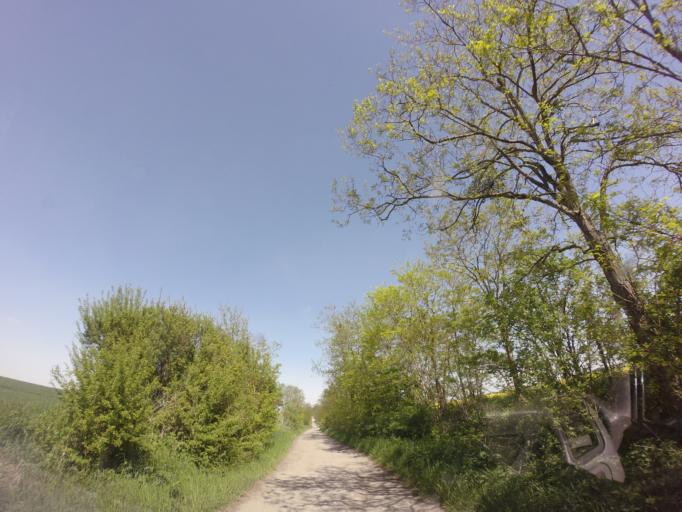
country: PL
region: West Pomeranian Voivodeship
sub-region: Powiat choszczenski
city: Pelczyce
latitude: 53.0194
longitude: 15.3497
